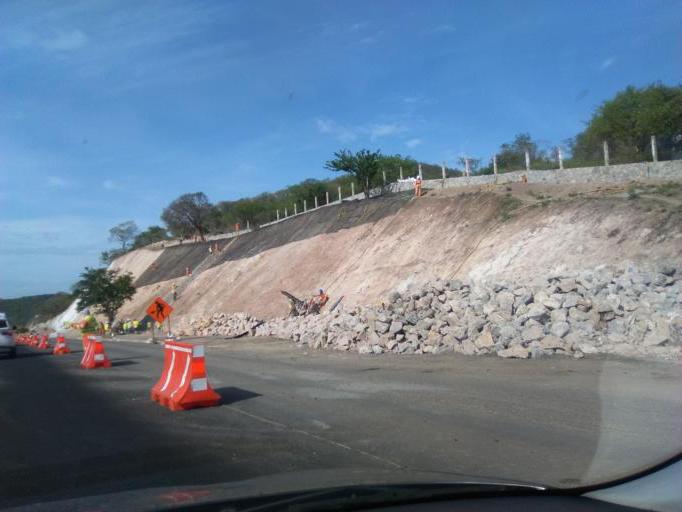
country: MX
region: Morelos
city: Tilzapotla
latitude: 18.4418
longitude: -99.1740
